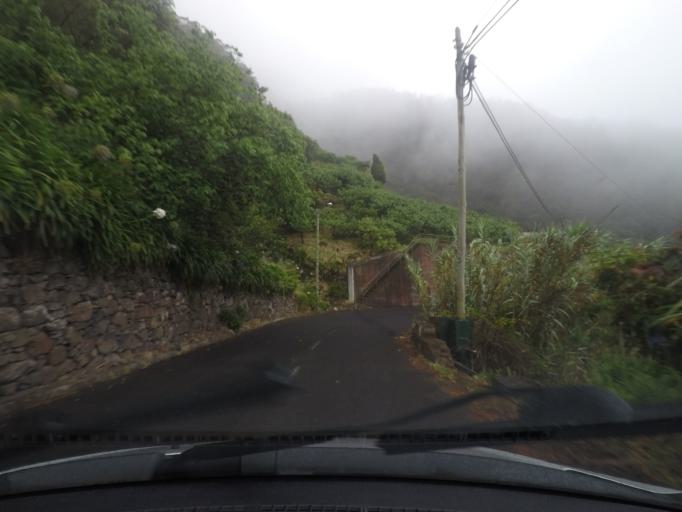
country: PT
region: Madeira
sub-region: Santana
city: Santana
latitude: 32.7822
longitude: -16.8614
